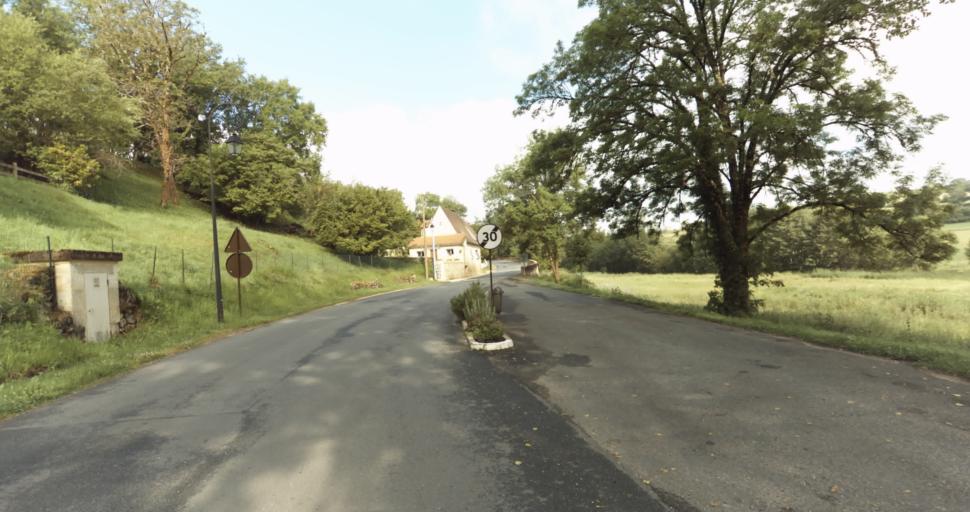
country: FR
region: Aquitaine
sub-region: Departement de la Dordogne
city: Lalinde
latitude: 44.9259
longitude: 0.7548
